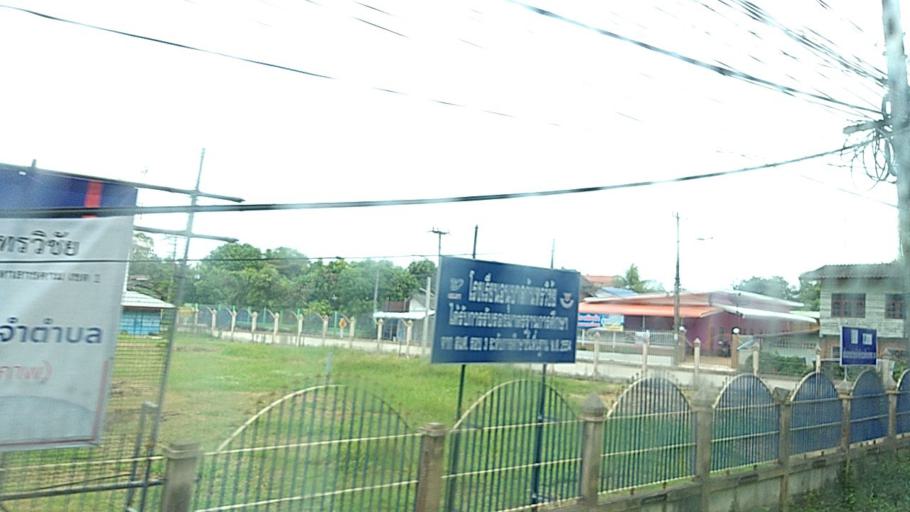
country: TH
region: Maha Sarakham
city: Kantharawichai
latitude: 16.3256
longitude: 103.2965
